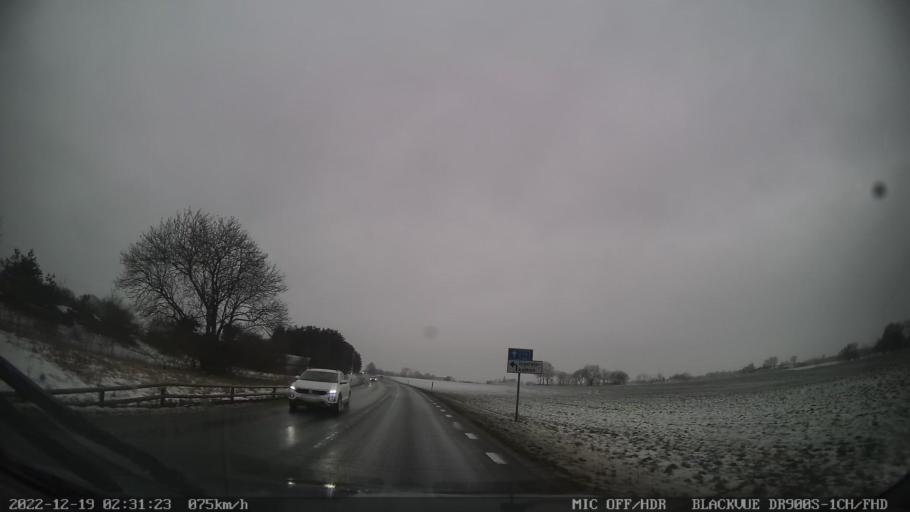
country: SE
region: Skane
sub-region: Tomelilla Kommun
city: Tomelilla
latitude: 55.5544
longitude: 14.0841
